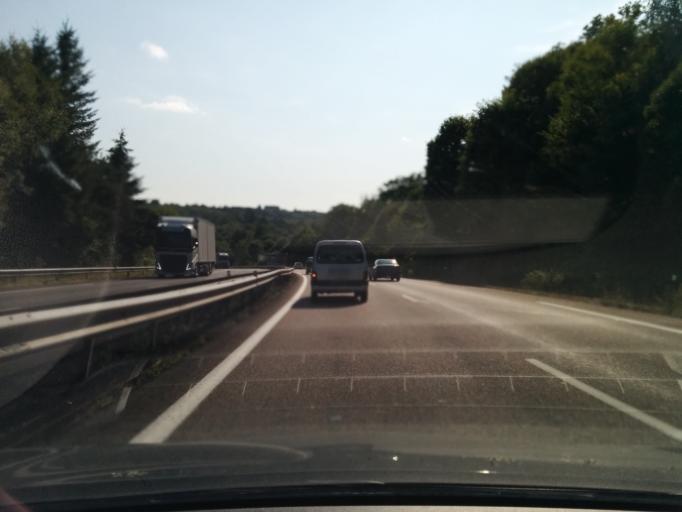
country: FR
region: Limousin
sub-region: Departement de la Haute-Vienne
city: Razes
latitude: 45.9923
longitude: 1.3291
